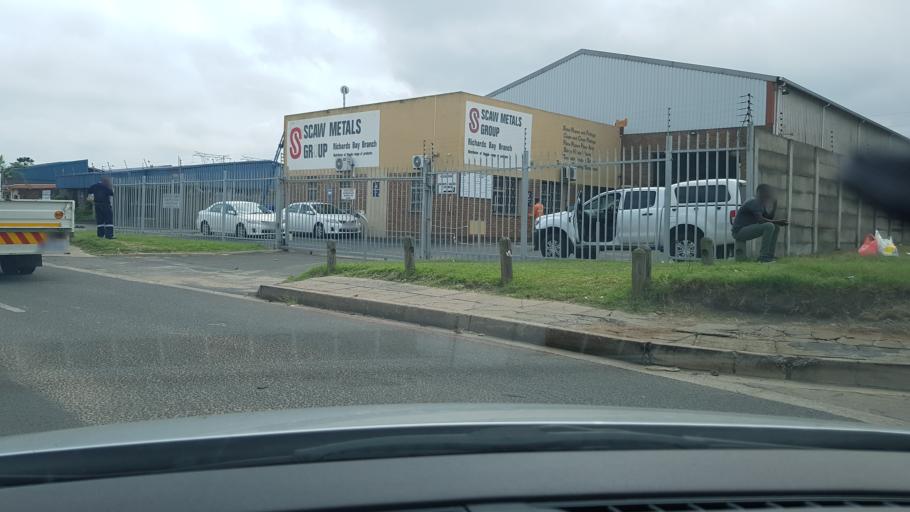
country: ZA
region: KwaZulu-Natal
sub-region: uThungulu District Municipality
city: Richards Bay
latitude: -28.7513
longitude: 32.0457
